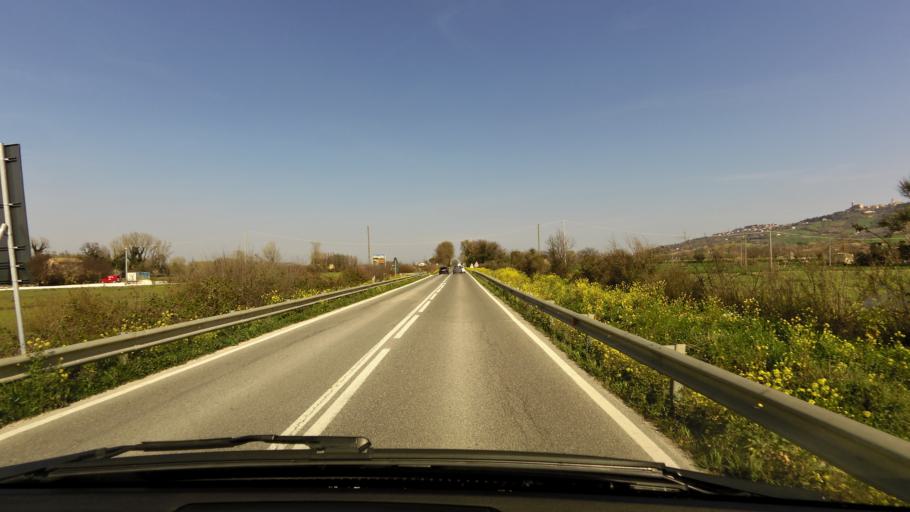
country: IT
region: The Marches
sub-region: Provincia di Macerata
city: Potenza Picena
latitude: 43.3722
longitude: 13.5894
